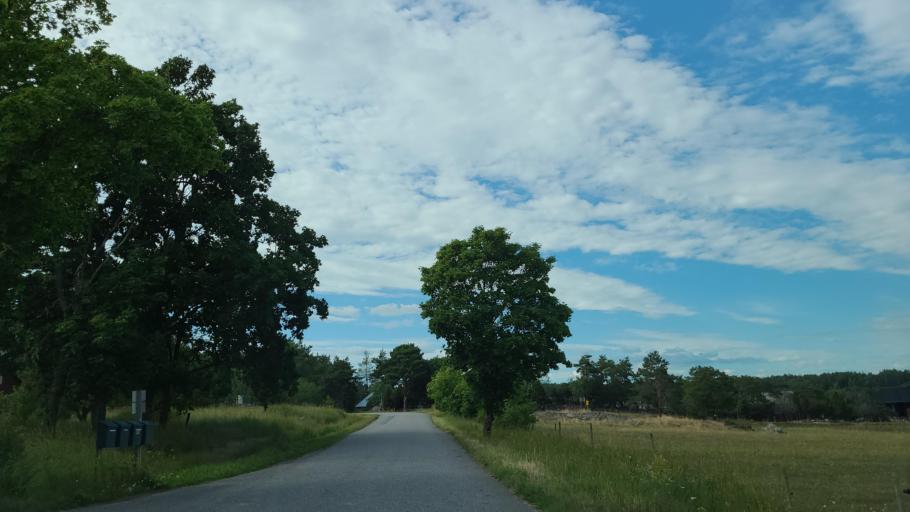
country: FI
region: Varsinais-Suomi
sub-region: Turku
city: Rymaettylae
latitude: 60.2924
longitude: 21.9398
